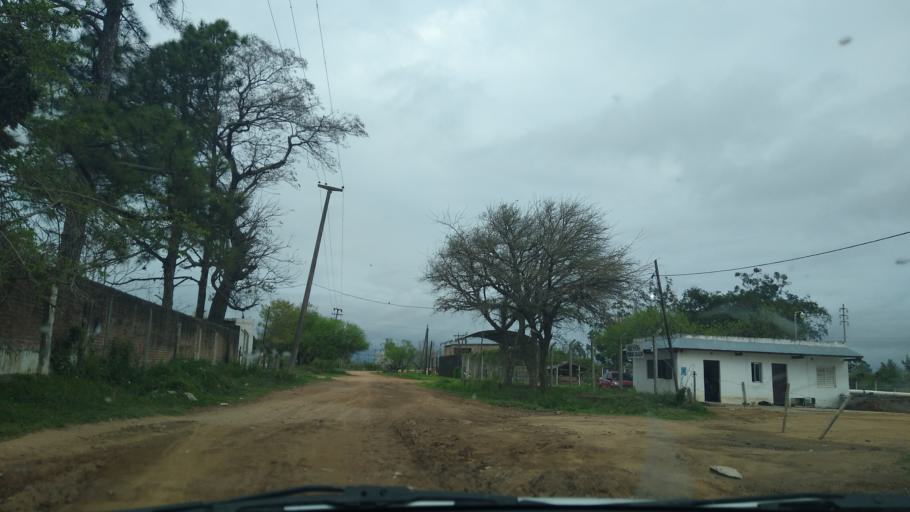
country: AR
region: Chaco
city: Barranqueras
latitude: -27.4741
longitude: -58.9121
